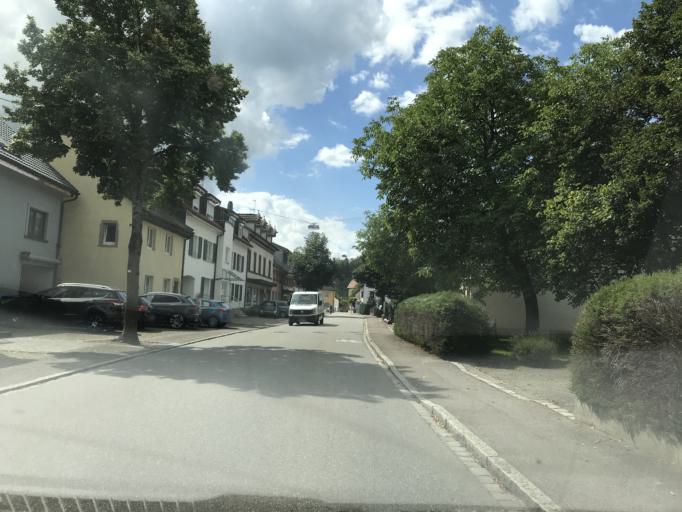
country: DE
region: Baden-Wuerttemberg
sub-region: Freiburg Region
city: Maulburg
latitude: 47.6431
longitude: 7.7802
